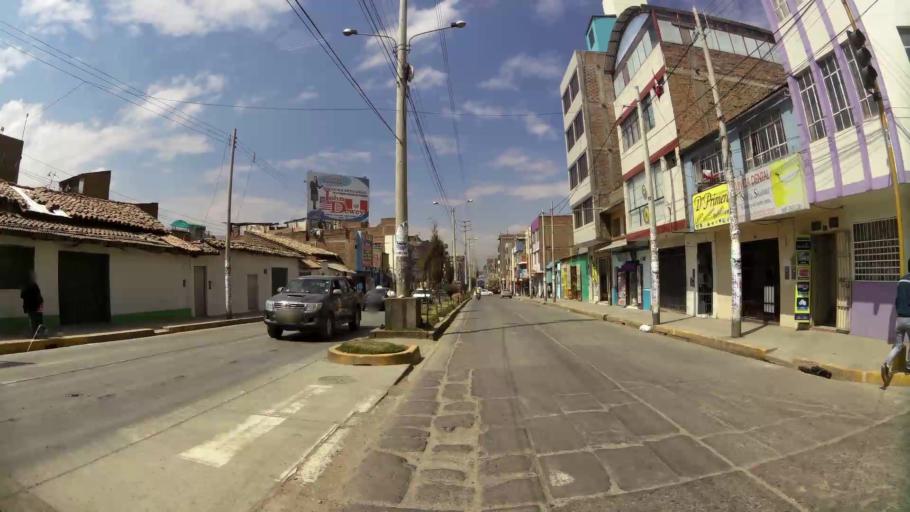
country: PE
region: Junin
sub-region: Provincia de Huancayo
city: El Tambo
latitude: -12.0717
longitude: -75.2139
